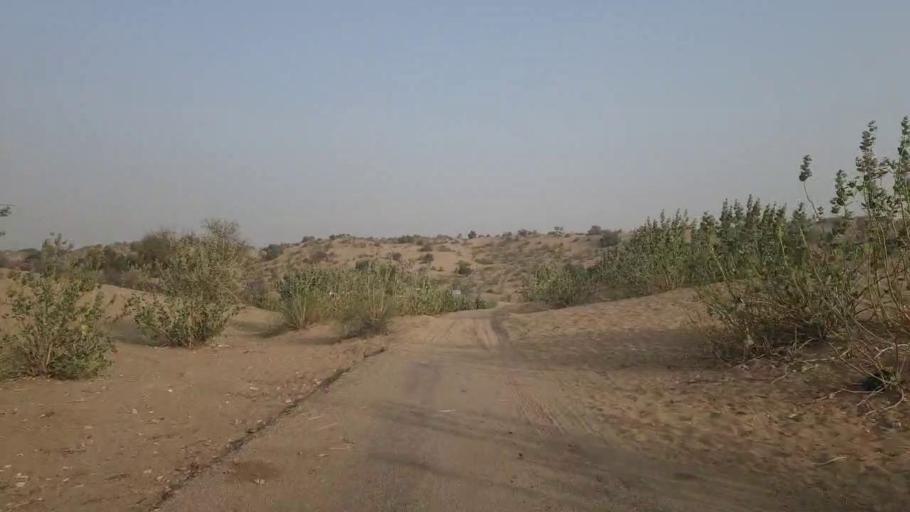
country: PK
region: Sindh
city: Chor
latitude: 25.5110
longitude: 70.0077
